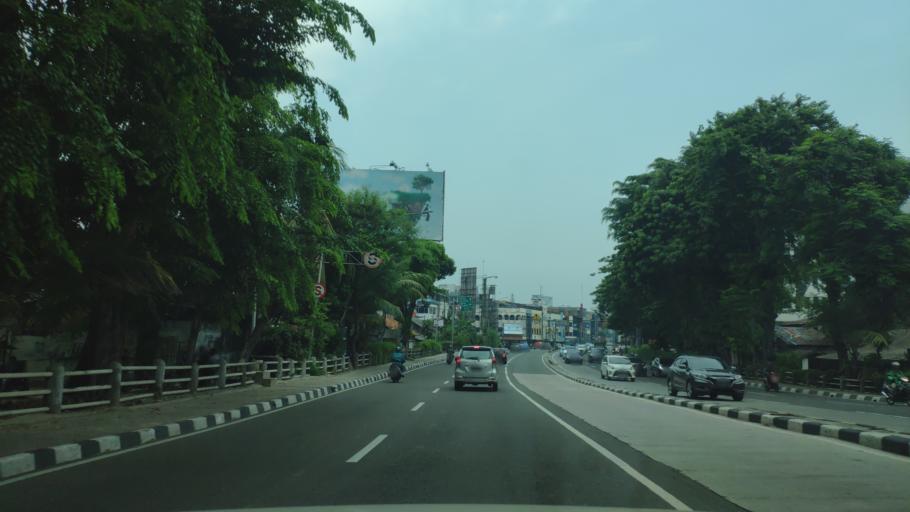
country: ID
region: Jakarta Raya
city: Jakarta
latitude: -6.1722
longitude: 106.8072
